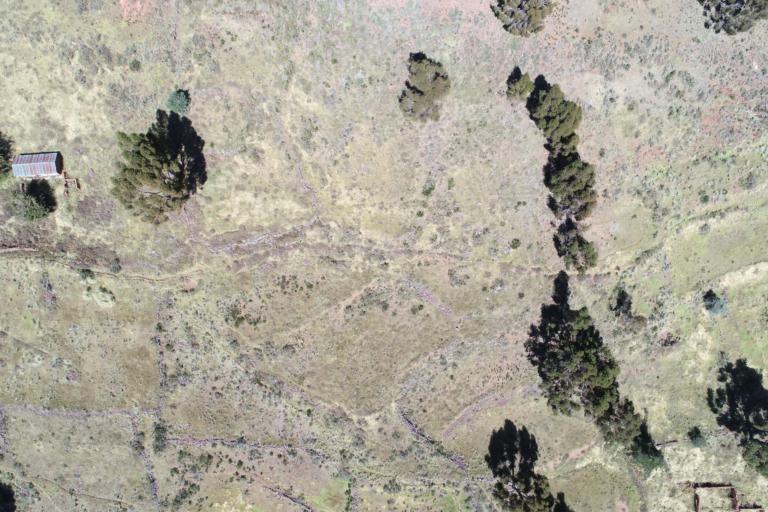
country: BO
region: La Paz
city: Tiahuanaco
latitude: -16.6040
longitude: -68.7742
